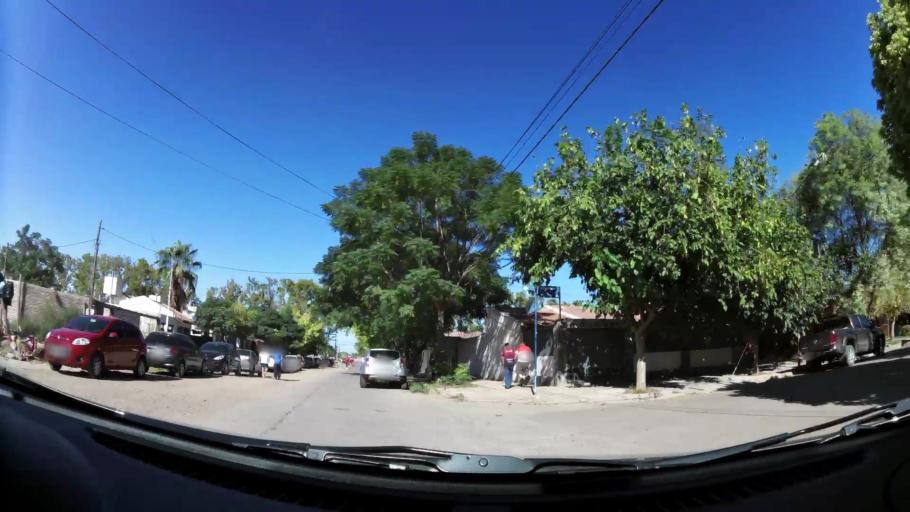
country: AR
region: Mendoza
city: Las Heras
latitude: -32.8476
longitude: -68.8289
